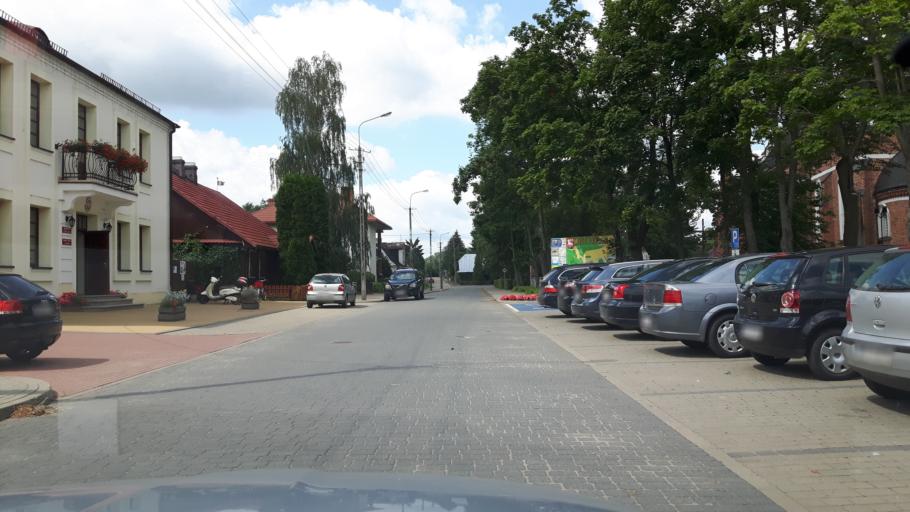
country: PL
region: Masovian Voivodeship
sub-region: Powiat ostrowski
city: Brok
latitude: 52.6985
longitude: 21.8629
